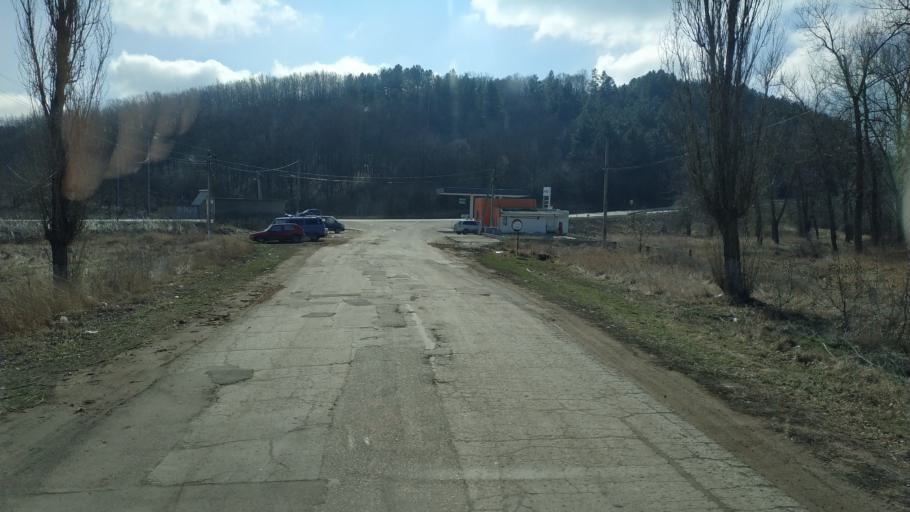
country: MD
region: Hincesti
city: Hincesti
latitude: 46.8683
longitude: 28.6389
